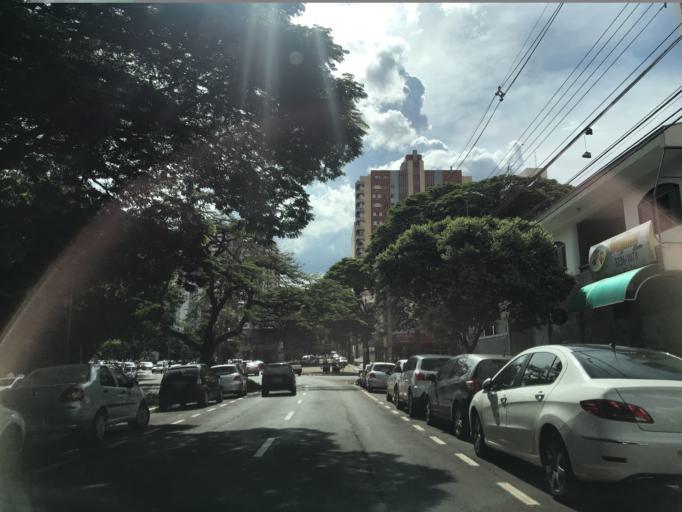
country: BR
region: Parana
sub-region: Maringa
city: Maringa
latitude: -23.4229
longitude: -51.9302
